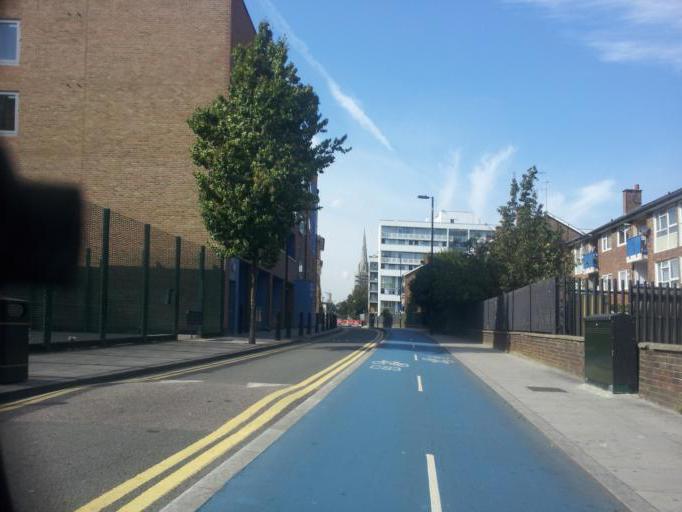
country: GB
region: England
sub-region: Greater London
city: Bethnal Green
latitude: 51.5115
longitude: -0.0461
